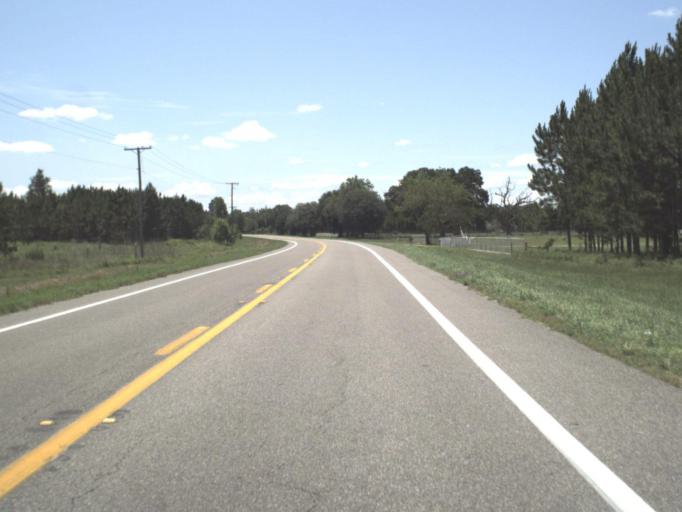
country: US
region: Florida
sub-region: Lafayette County
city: Mayo
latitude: 30.0493
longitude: -83.0842
